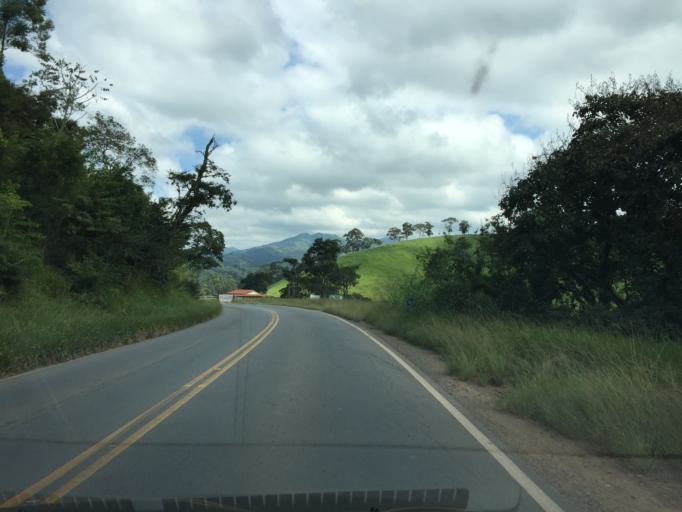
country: BR
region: Minas Gerais
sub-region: Passa Quatro
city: Passa Quatro
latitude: -22.3698
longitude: -44.9618
